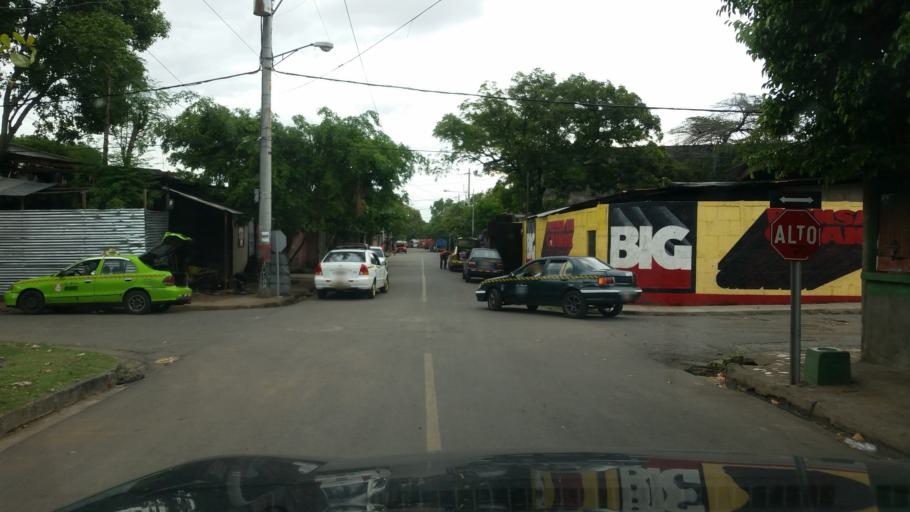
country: NI
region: Managua
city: Managua
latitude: 12.1472
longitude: -86.2668
